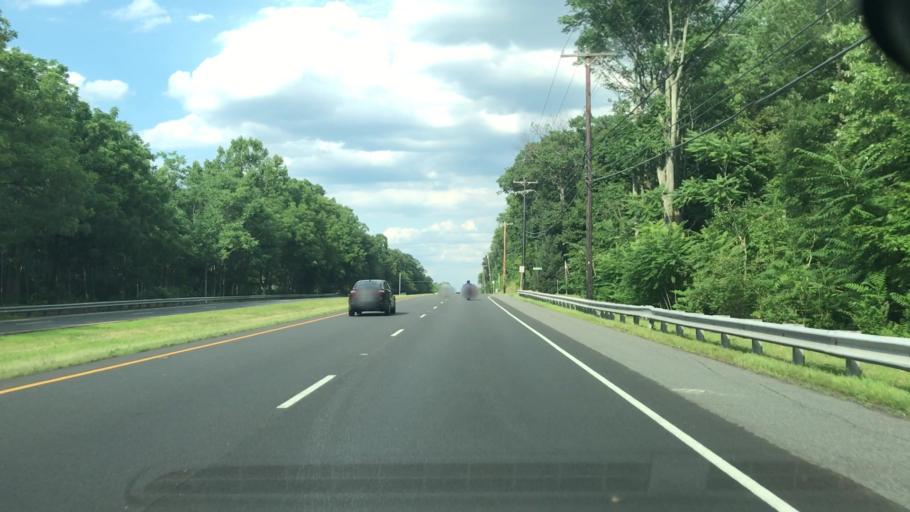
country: US
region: New Jersey
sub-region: Somerset County
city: Bradley Gardens
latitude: 40.5539
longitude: -74.7220
